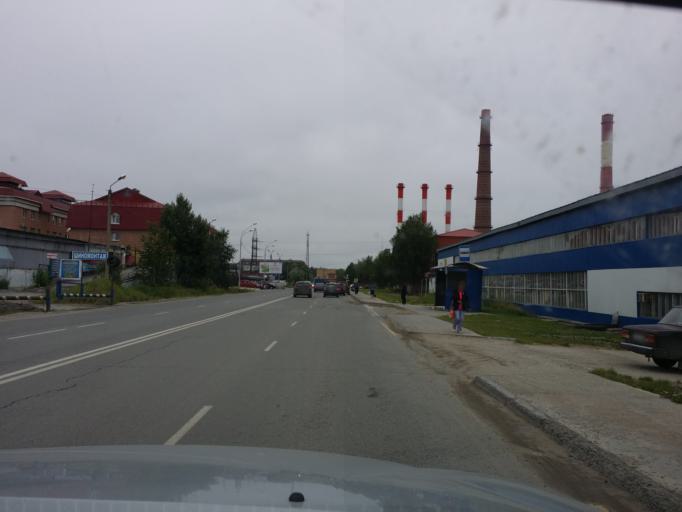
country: RU
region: Khanty-Mansiyskiy Avtonomnyy Okrug
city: Nizhnevartovsk
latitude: 60.9359
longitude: 76.5488
